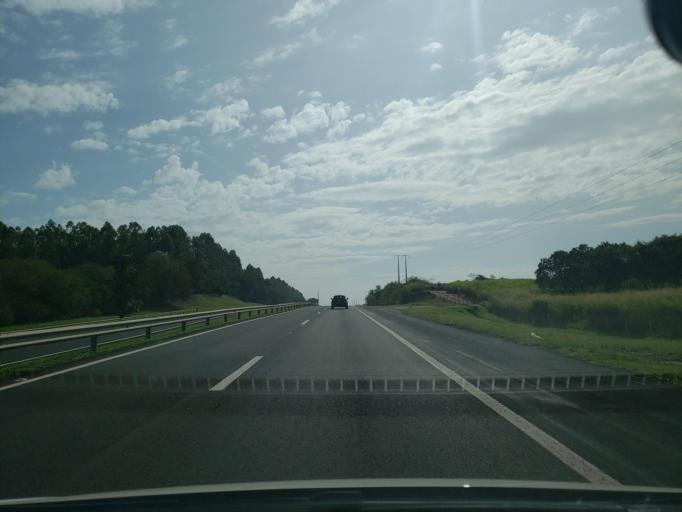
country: BR
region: Sao Paulo
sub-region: Lins
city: Lins
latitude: -21.7244
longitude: -49.7181
